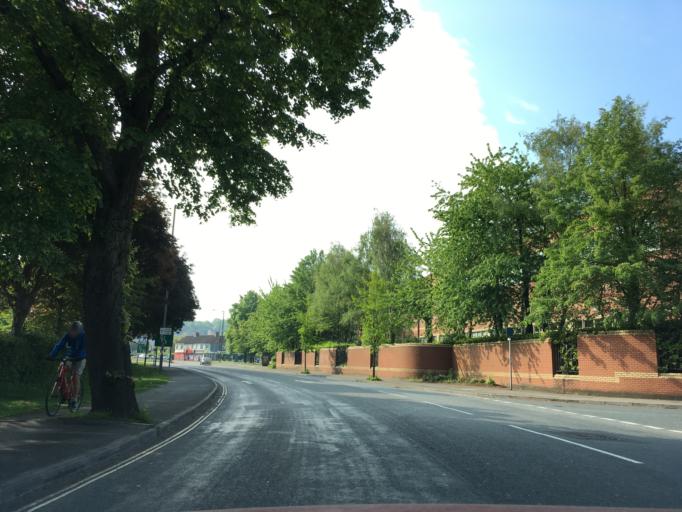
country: GB
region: England
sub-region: Bristol
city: Bristol
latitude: 51.4363
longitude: -2.6202
